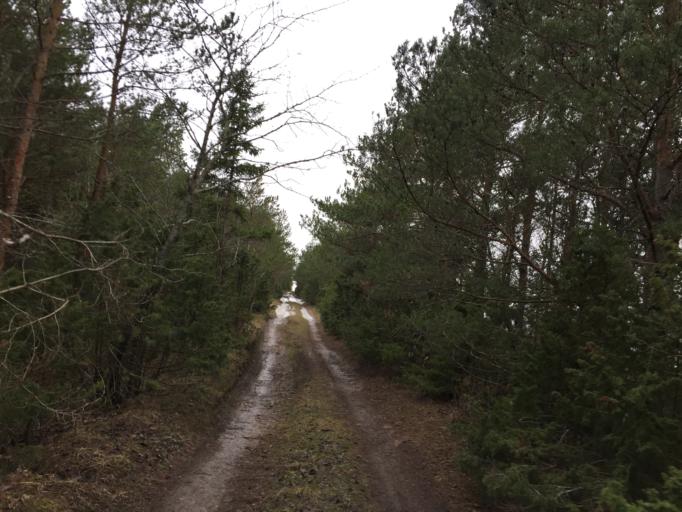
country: EE
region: Saare
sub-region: Kuressaare linn
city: Kuressaare
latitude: 58.5464
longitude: 22.2099
